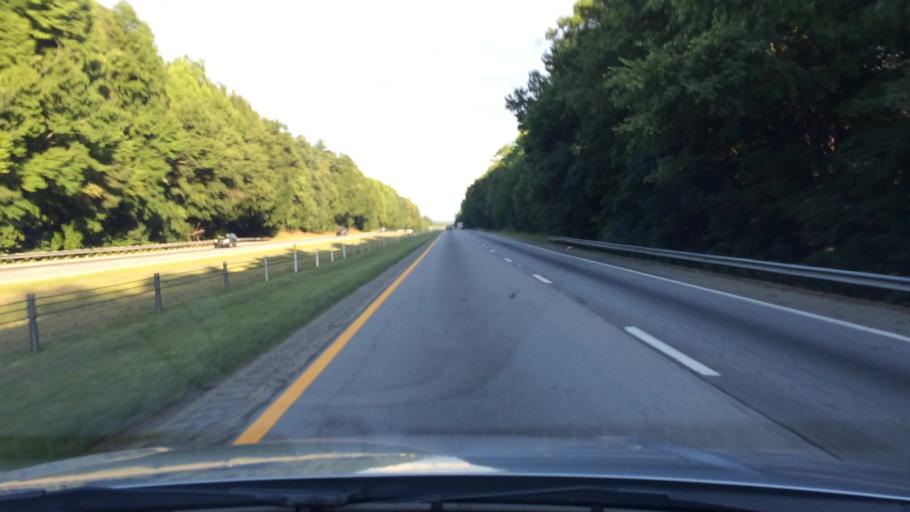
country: US
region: South Carolina
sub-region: Lexington County
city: Chapin
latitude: 34.1985
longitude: -81.3605
